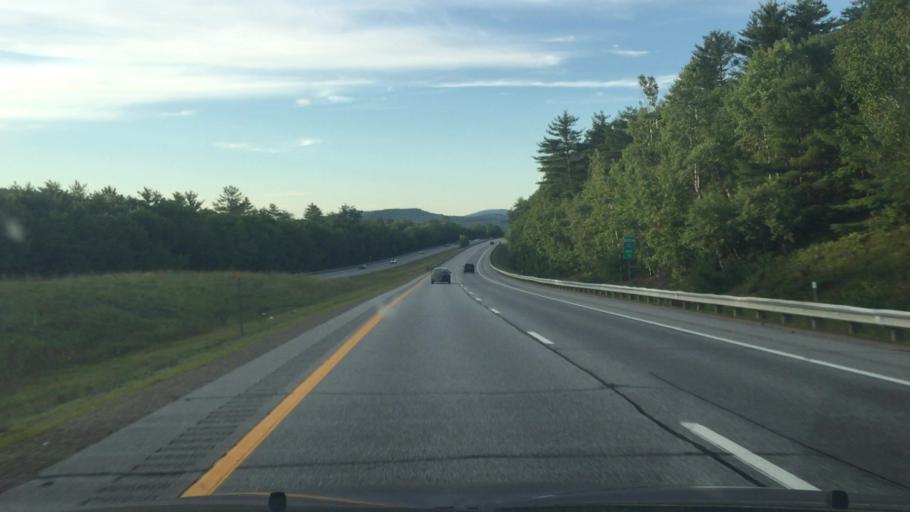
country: US
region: New Hampshire
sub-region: Grafton County
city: Ashland
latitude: 43.6654
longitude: -71.6491
